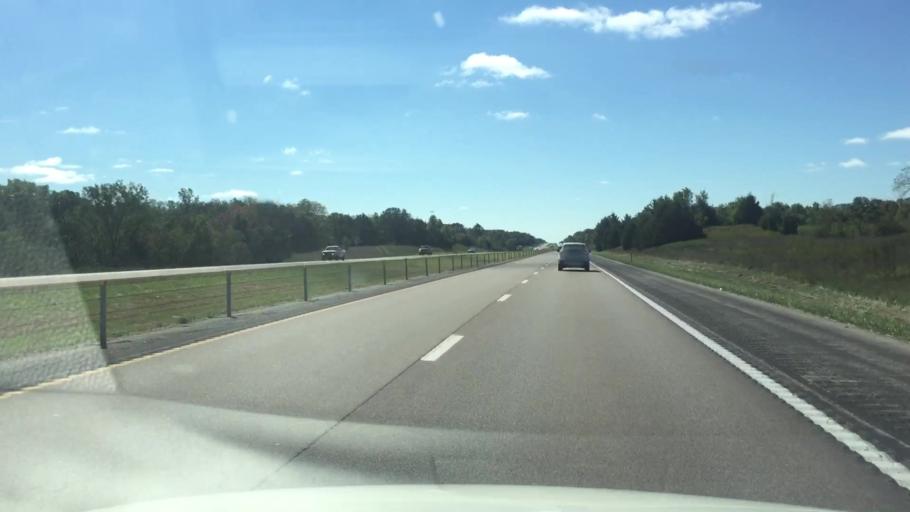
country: US
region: Missouri
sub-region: Boone County
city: Ashland
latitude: 38.7406
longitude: -92.2538
